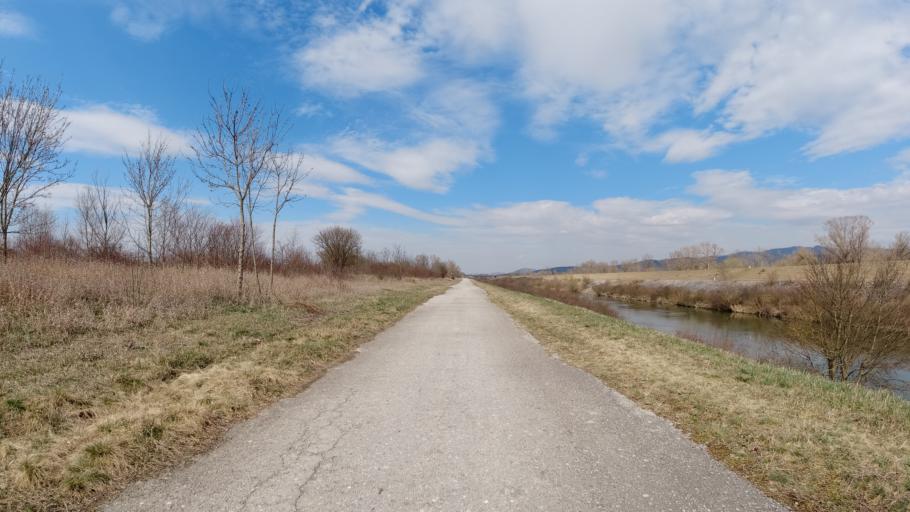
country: SK
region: Trnavsky
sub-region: Okres Trnava
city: Piestany
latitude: 48.6345
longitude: 17.8437
